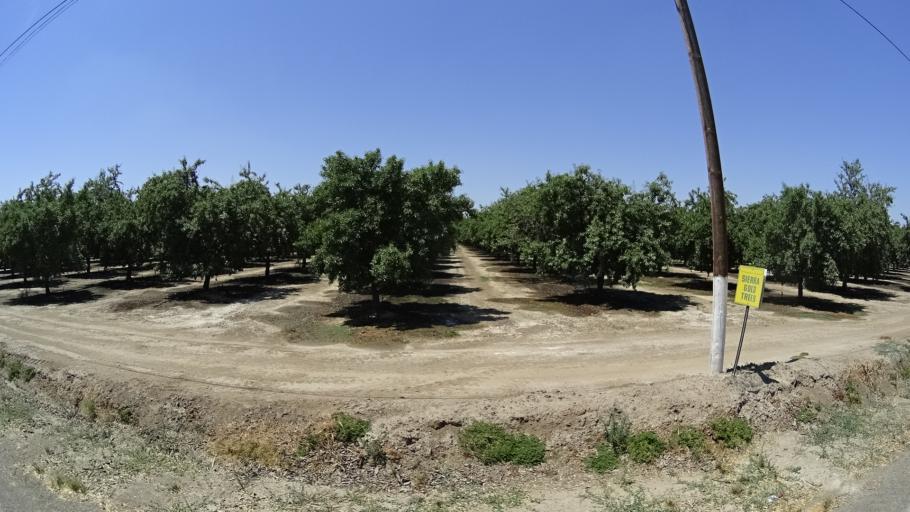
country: US
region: California
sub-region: Kings County
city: Armona
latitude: 36.3304
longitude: -119.7269
